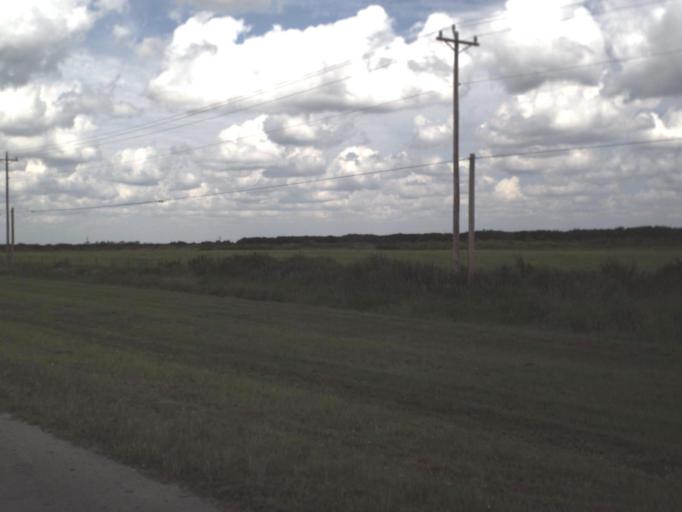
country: US
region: Florida
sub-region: Collier County
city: Immokalee
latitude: 26.4471
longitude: -81.4340
